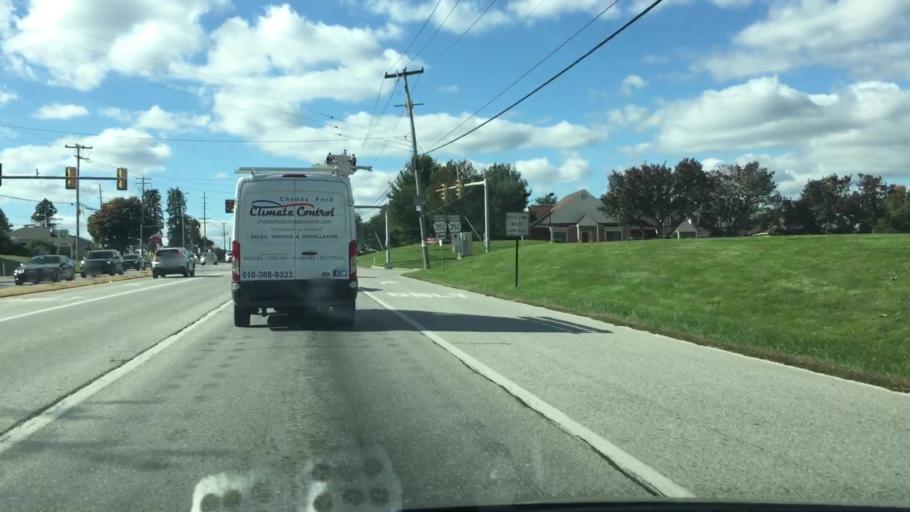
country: US
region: Pennsylvania
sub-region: Chester County
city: Malvern
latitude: 39.9664
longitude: -75.5194
